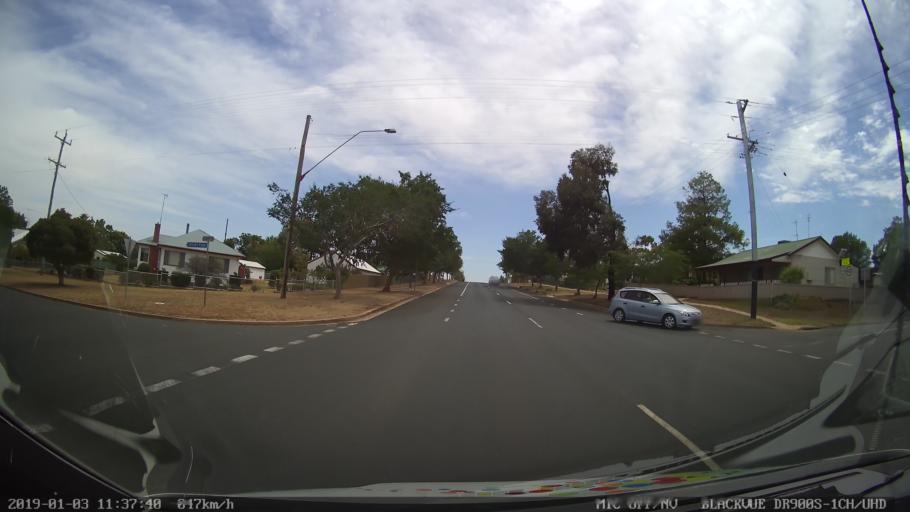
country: AU
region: New South Wales
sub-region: Weddin
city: Grenfell
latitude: -33.9015
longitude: 148.1615
